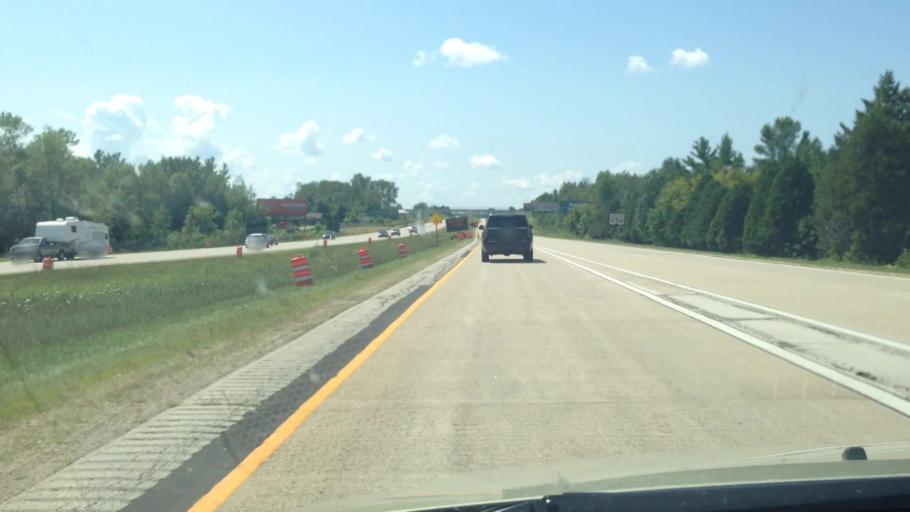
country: US
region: Wisconsin
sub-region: Oconto County
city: Oconto Falls
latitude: 44.7849
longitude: -88.0469
